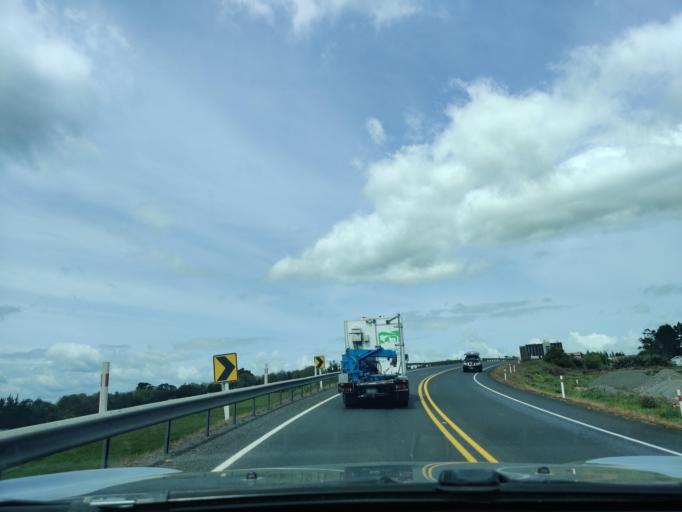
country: NZ
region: Taranaki
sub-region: South Taranaki District
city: Eltham
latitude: -39.2824
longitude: 174.2648
